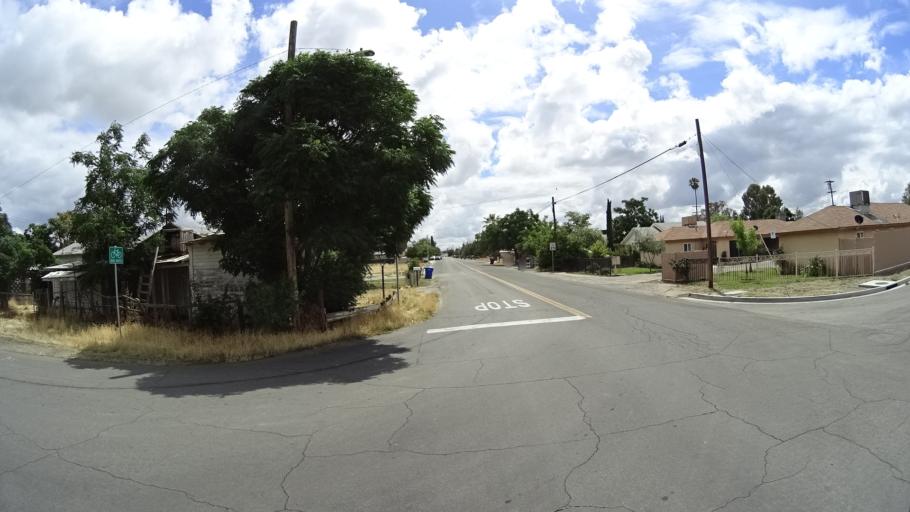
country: US
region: California
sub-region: Kings County
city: Hanford
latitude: 36.3242
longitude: -119.6642
